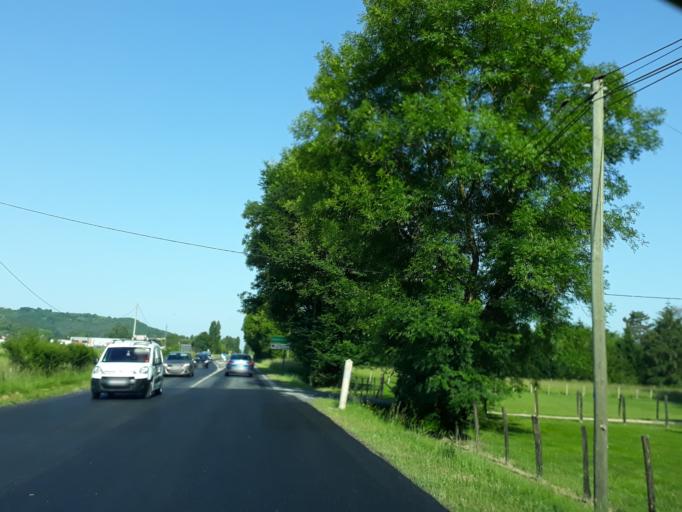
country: FR
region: Limousin
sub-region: Departement de la Correze
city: Larche
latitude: 45.1252
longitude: 1.4009
